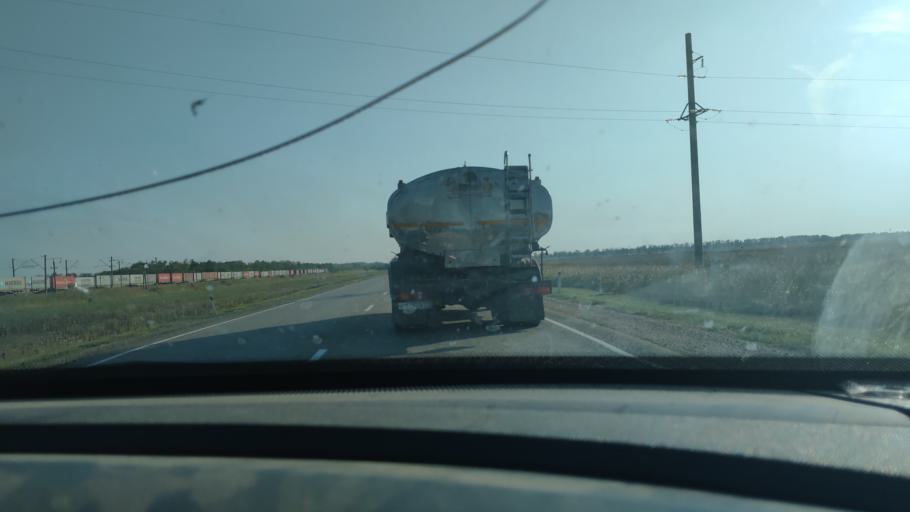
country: RU
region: Krasnodarskiy
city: Starominskaya
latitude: 46.4397
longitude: 39.0222
